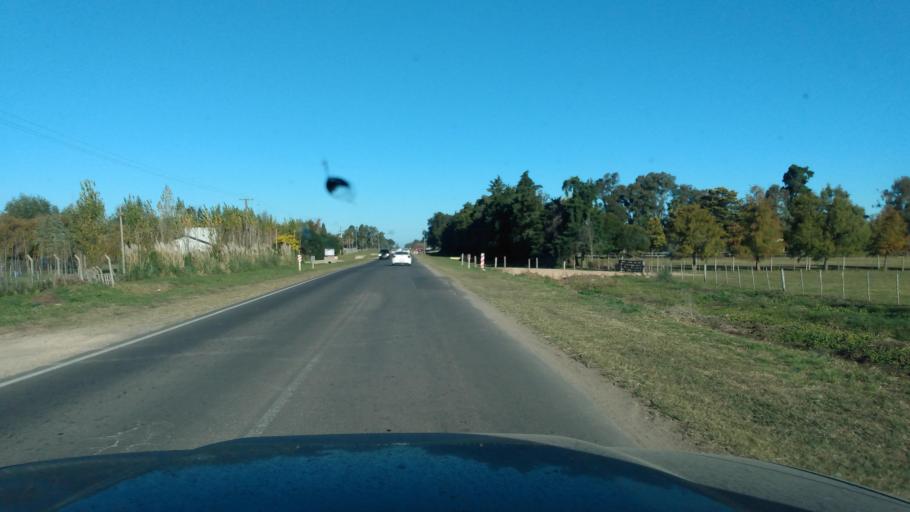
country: AR
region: Buenos Aires
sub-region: Partido de Lujan
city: Lujan
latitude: -34.5073
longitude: -59.1860
